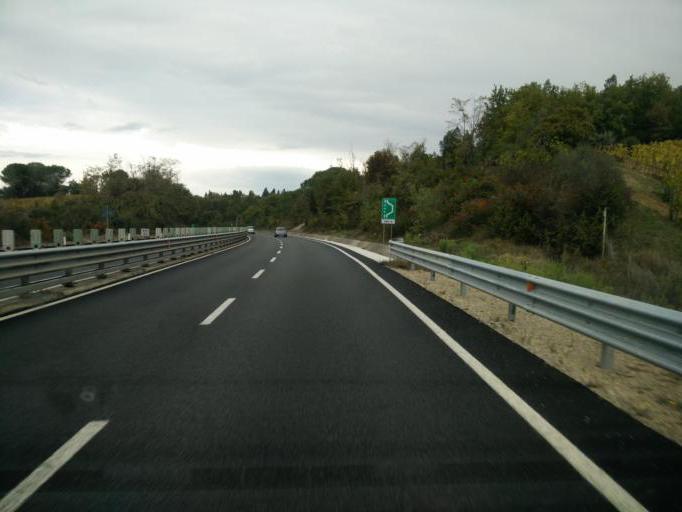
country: IT
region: Tuscany
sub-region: Province of Florence
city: Sambuca
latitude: 43.5390
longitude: 11.2204
